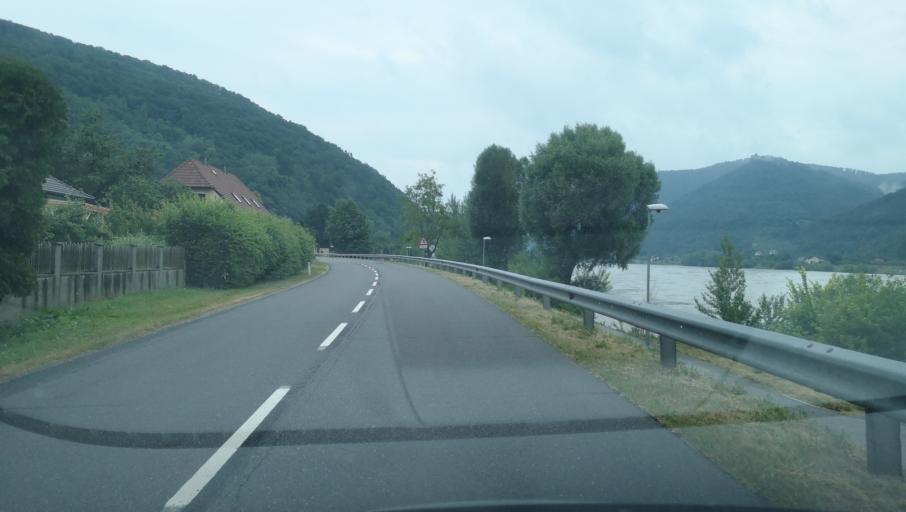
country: AT
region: Lower Austria
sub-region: Politischer Bezirk Krems
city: Aggsbach
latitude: 48.2957
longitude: 15.4049
